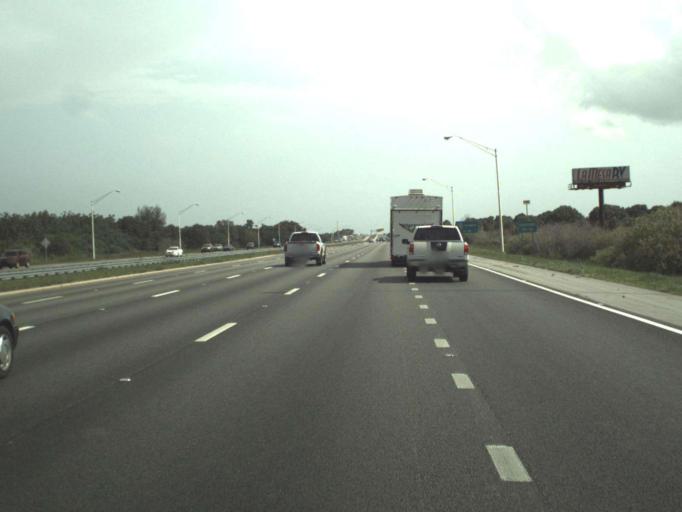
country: US
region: Florida
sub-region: Saint Lucie County
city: Fort Pierce South
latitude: 27.4271
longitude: -80.3886
